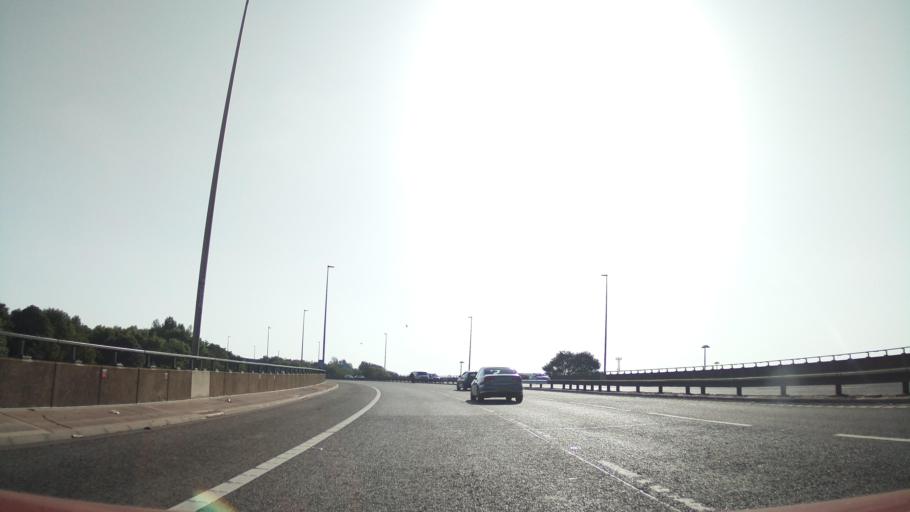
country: GB
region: England
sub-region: Sandwell
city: Smethwick
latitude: 52.5058
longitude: -1.9829
